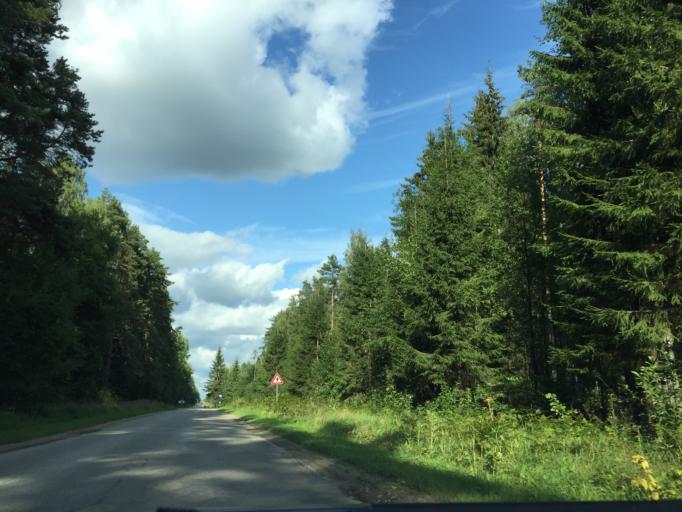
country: LV
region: Ogre
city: Ogre
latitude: 56.8278
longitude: 24.6420
